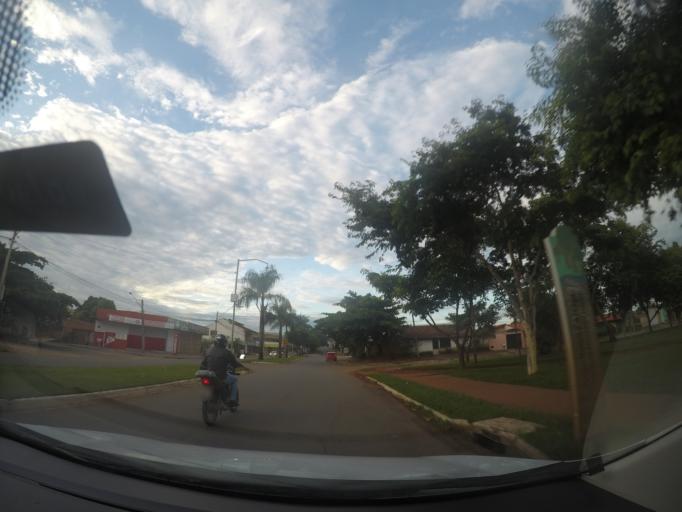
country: BR
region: Goias
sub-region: Goiania
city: Goiania
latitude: -16.6920
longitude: -49.3509
